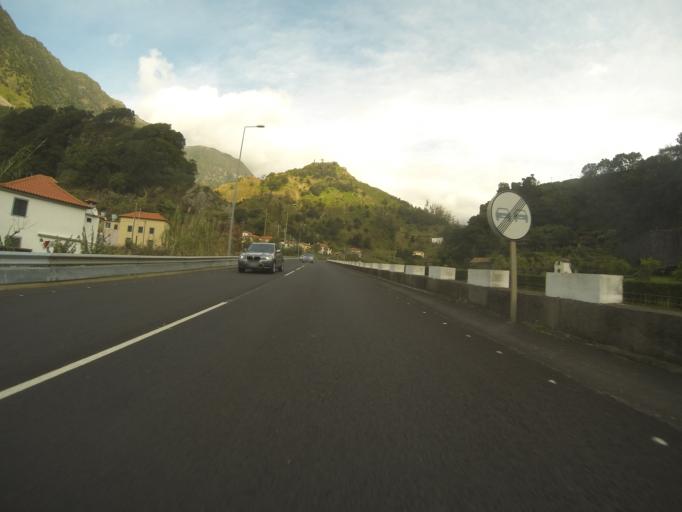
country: PT
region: Madeira
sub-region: Sao Vicente
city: Sao Vicente
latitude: 32.7979
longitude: -17.0418
